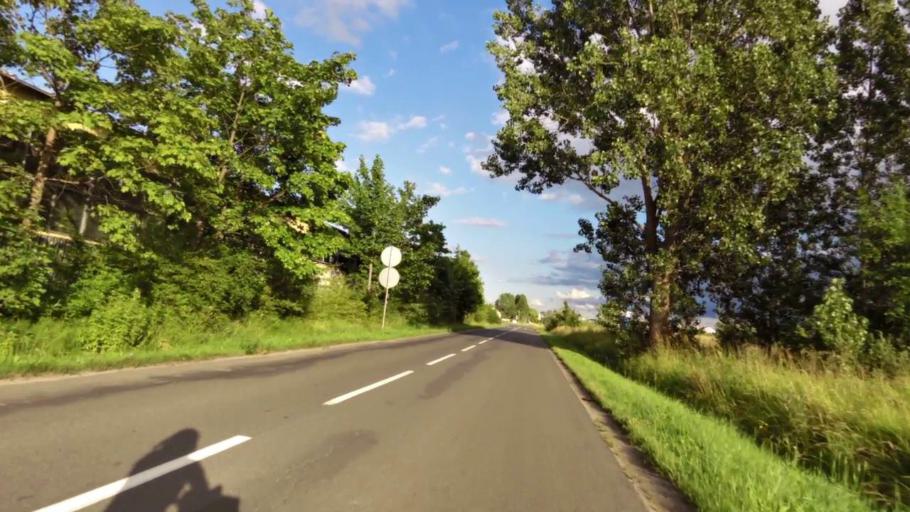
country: PL
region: West Pomeranian Voivodeship
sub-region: Powiat slawienski
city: Darlowo
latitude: 54.4142
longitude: 16.4034
